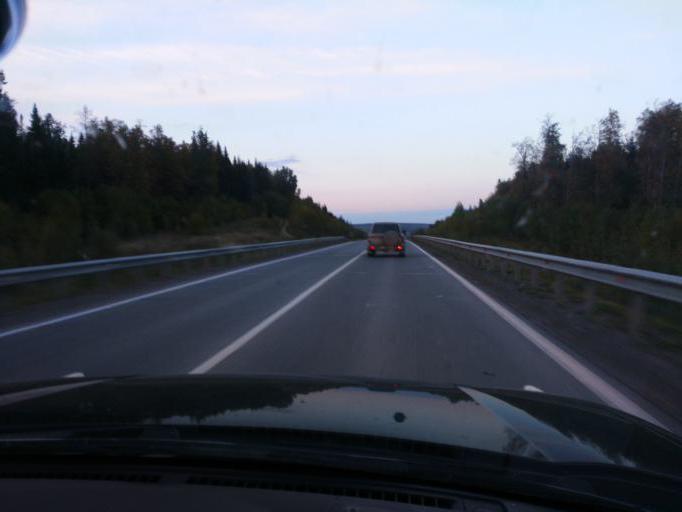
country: RU
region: Perm
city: Sylva
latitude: 58.2904
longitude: 56.7478
